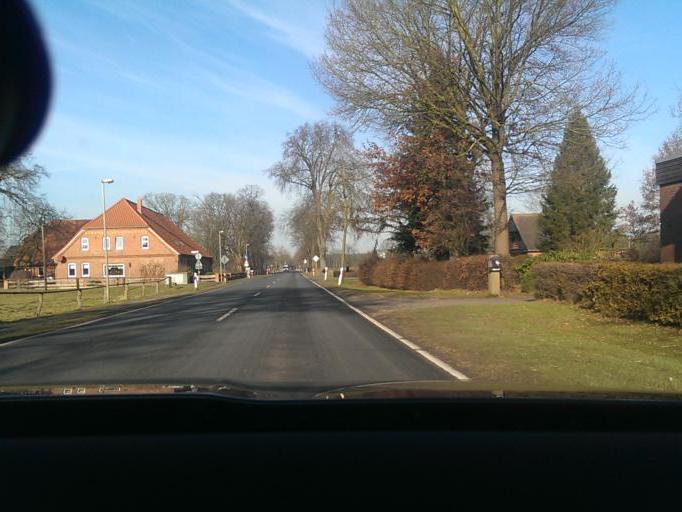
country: DE
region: Lower Saxony
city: Elze
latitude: 52.6077
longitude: 9.7193
